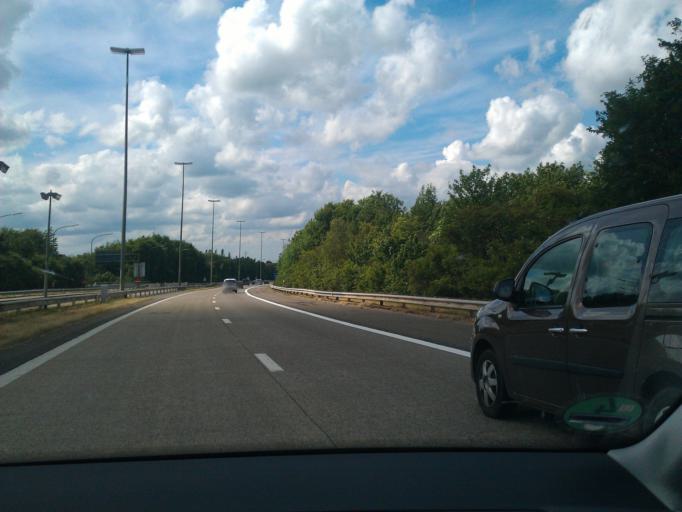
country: BE
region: Wallonia
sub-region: Province de Liege
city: Verviers
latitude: 50.5550
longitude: 5.8616
